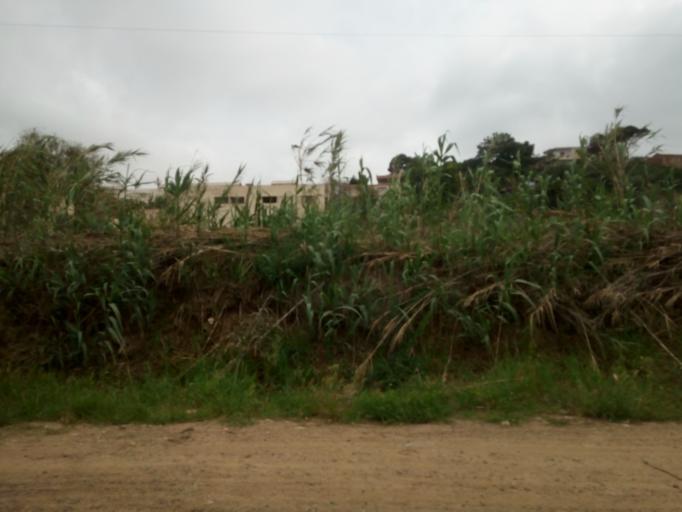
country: DZ
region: Tipaza
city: Tipasa
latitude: 36.5895
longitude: 2.5050
